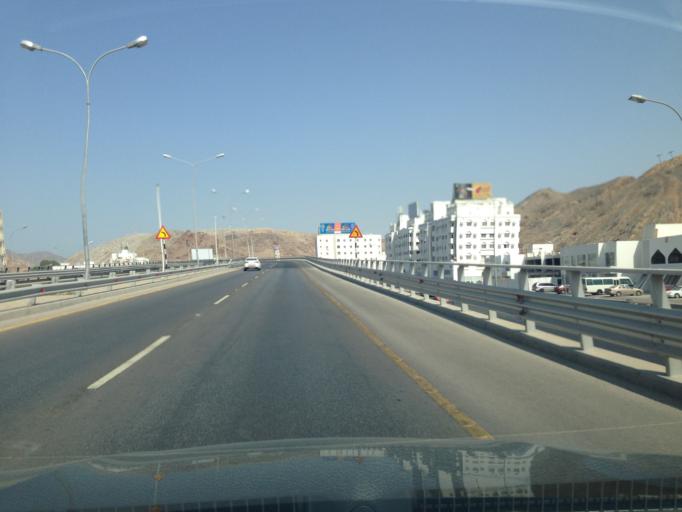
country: OM
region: Muhafazat Masqat
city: Muscat
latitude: 23.5871
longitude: 58.5361
